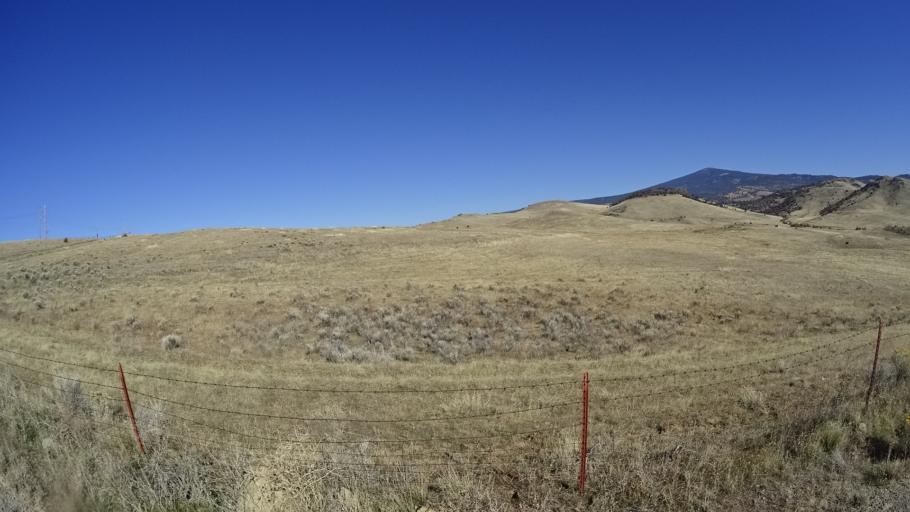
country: US
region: California
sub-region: Siskiyou County
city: Montague
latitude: 41.7674
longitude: -122.3577
